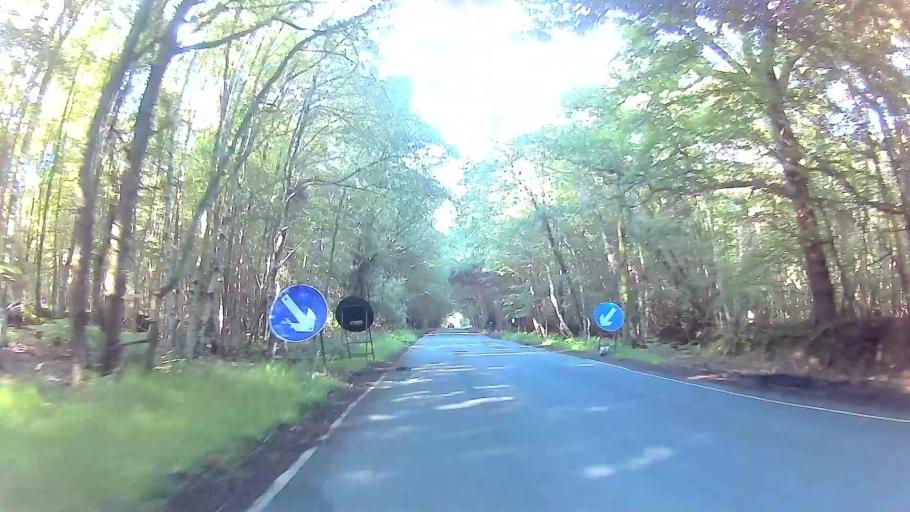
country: GB
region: England
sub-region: Essex
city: Ingatestone
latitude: 51.6994
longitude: 0.3511
